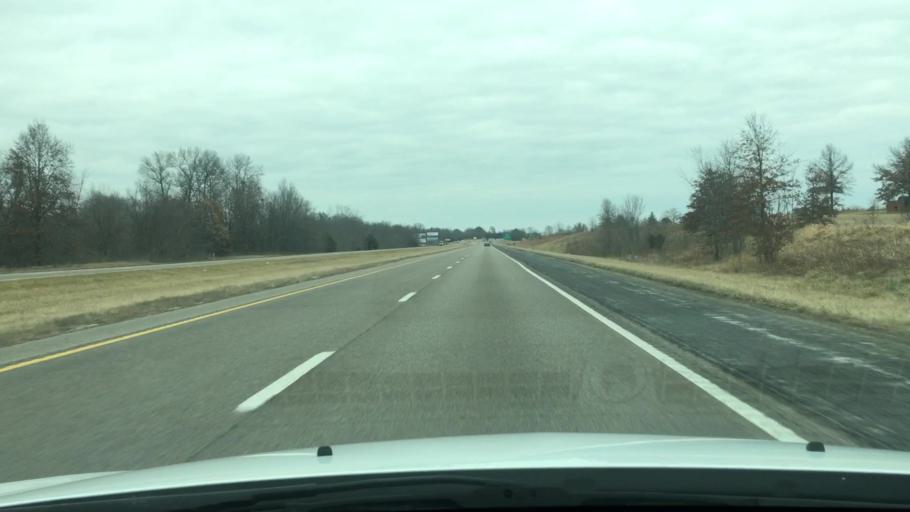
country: US
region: Missouri
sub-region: Callaway County
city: Fulton
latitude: 38.9969
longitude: -91.8934
